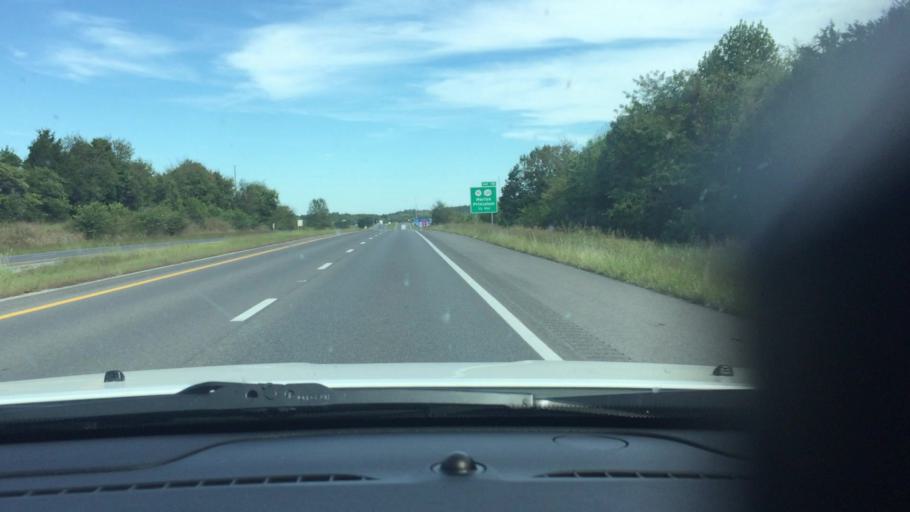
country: US
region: Kentucky
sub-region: Caldwell County
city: Princeton
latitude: 37.1189
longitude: -87.9104
